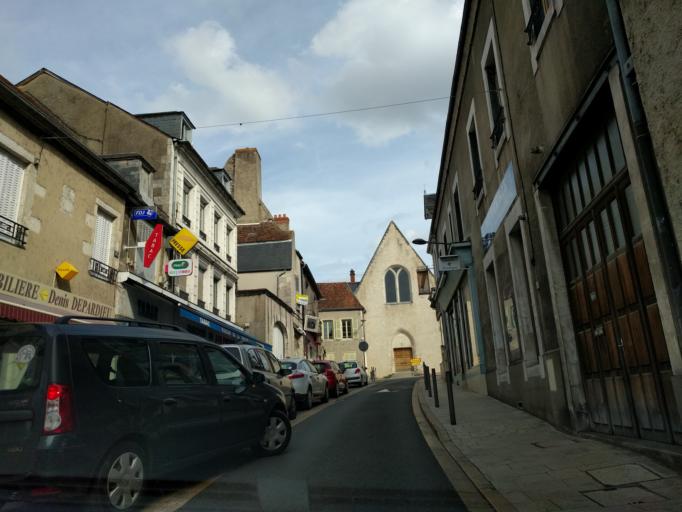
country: FR
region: Bourgogne
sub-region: Departement de la Nievre
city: La Charite-sur-Loire
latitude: 47.1774
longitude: 3.0203
